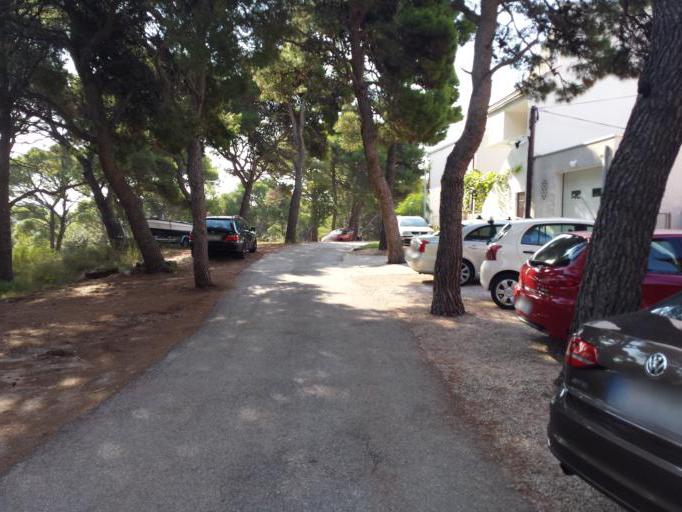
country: HR
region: Sibensko-Kniniska
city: Rogoznica
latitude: 43.5271
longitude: 15.9709
